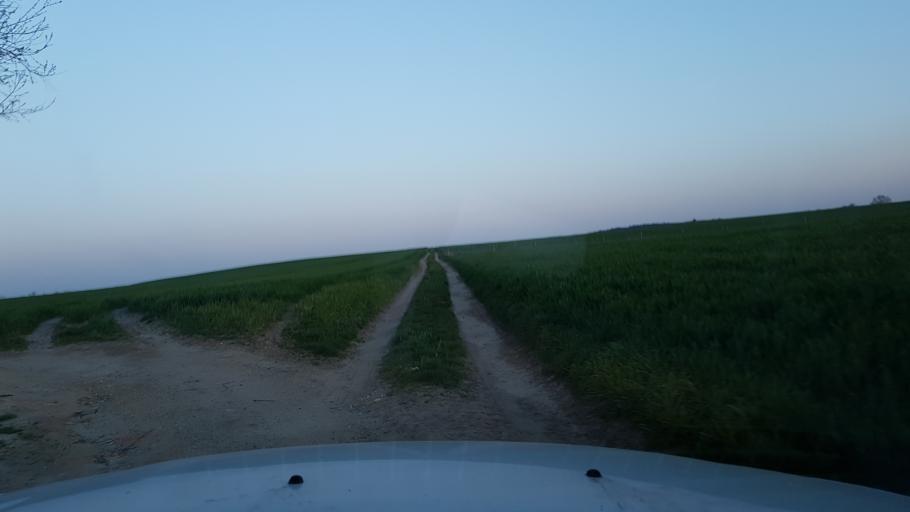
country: PL
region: West Pomeranian Voivodeship
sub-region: Powiat bialogardzki
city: Bialogard
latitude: 53.9611
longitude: 15.9580
